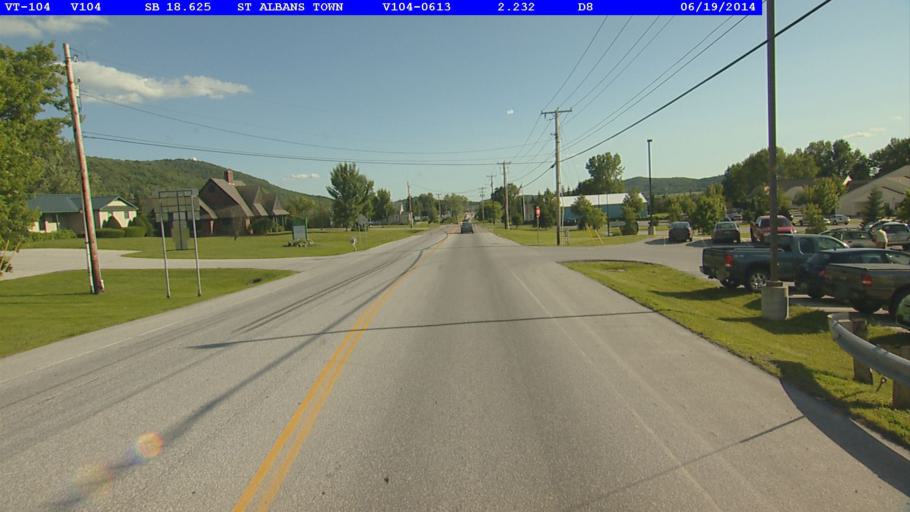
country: US
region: Vermont
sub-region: Franklin County
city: Saint Albans
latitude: 44.8047
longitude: -73.0691
